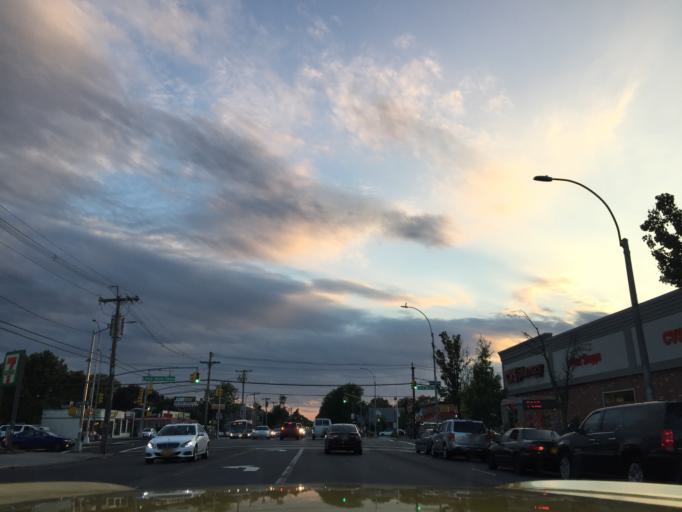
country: US
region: New York
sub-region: Nassau County
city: Bellerose
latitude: 40.7364
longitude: -73.7129
